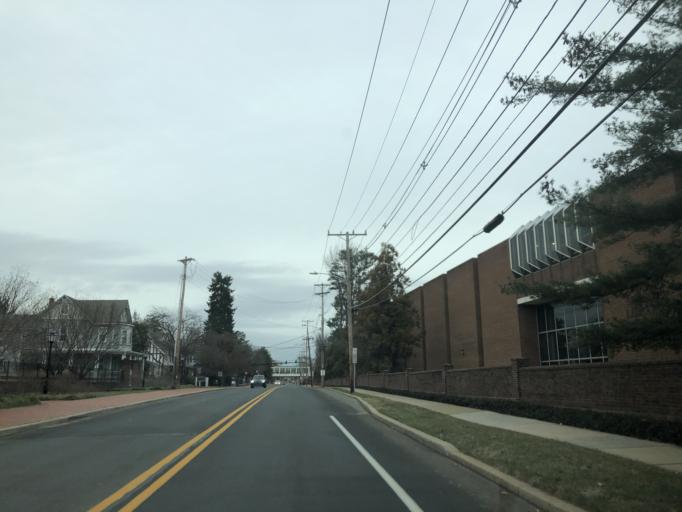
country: US
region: Delaware
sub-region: New Castle County
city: Newark
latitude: 39.6776
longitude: -75.7535
